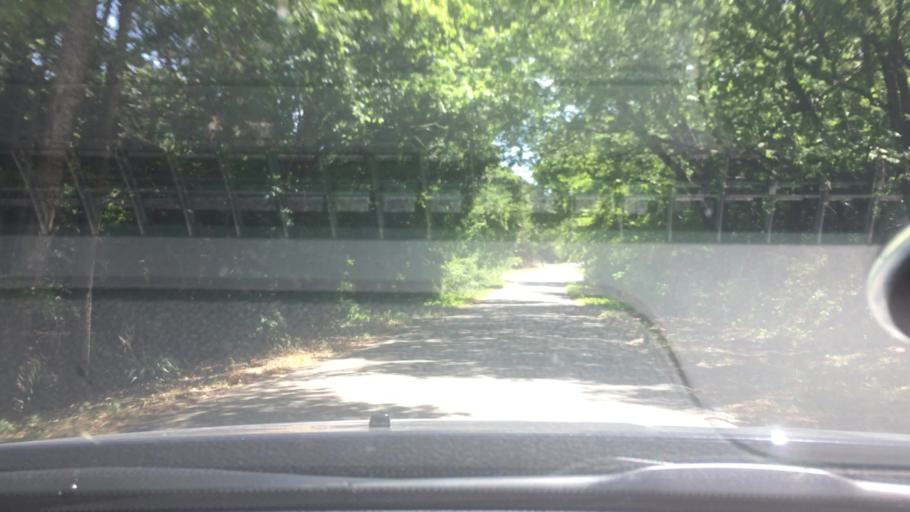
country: US
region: Oklahoma
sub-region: Bryan County
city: Durant
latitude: 33.9830
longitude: -96.2523
